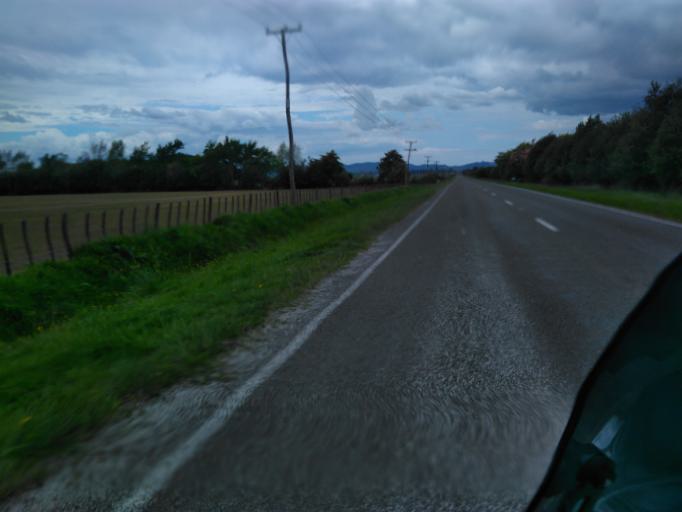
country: NZ
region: Gisborne
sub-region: Gisborne District
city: Gisborne
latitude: -38.6435
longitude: 177.8750
